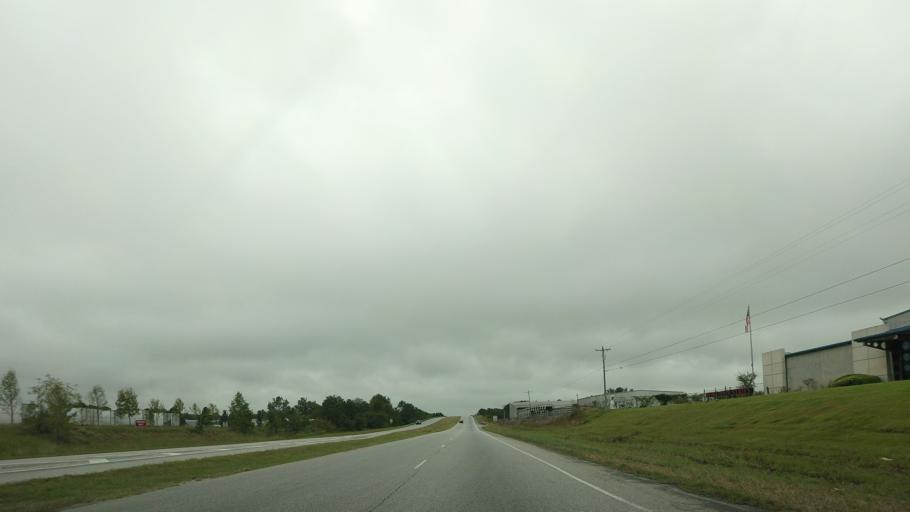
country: US
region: Georgia
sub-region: Lowndes County
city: Valdosta
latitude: 30.8351
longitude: -83.2281
